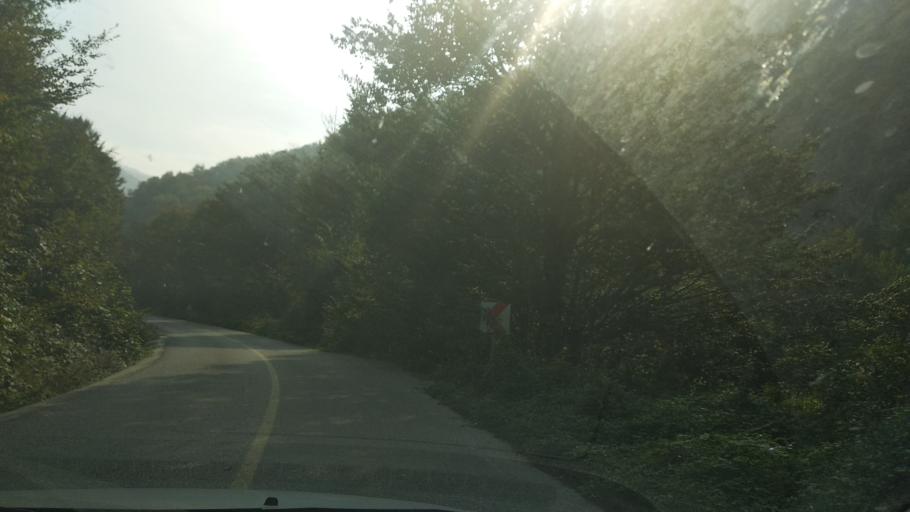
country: TR
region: Duzce
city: Kaynasli
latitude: 40.7070
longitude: 31.2647
